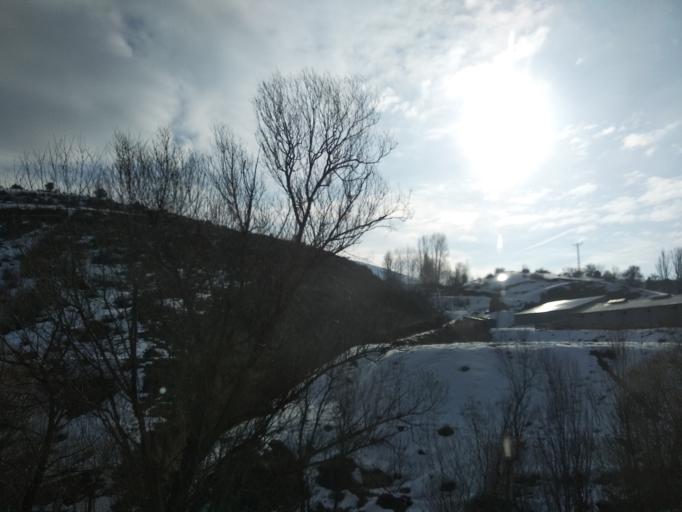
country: TR
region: Gumushane
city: Kelkit
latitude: 40.0622
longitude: 39.4983
